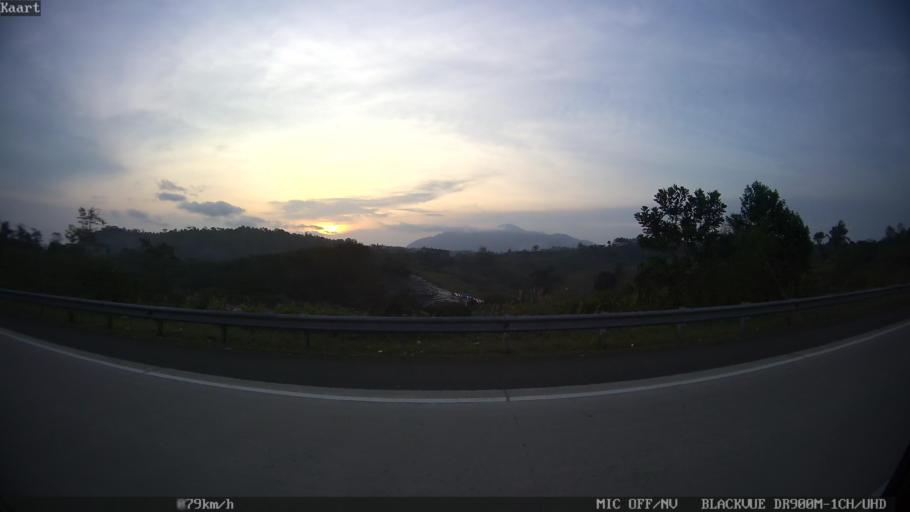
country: ID
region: Lampung
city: Penengahan
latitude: -5.8350
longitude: 105.7307
